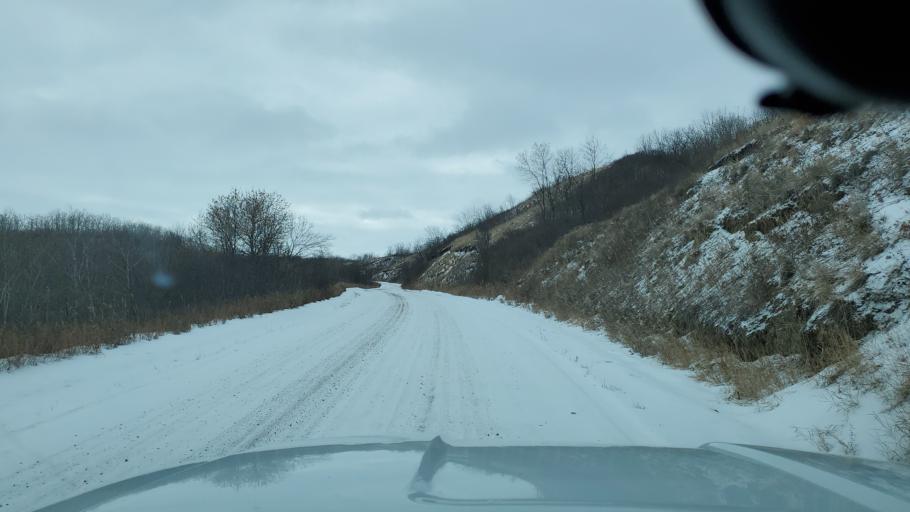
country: CA
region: Saskatchewan
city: White City
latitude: 50.7717
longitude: -104.1472
